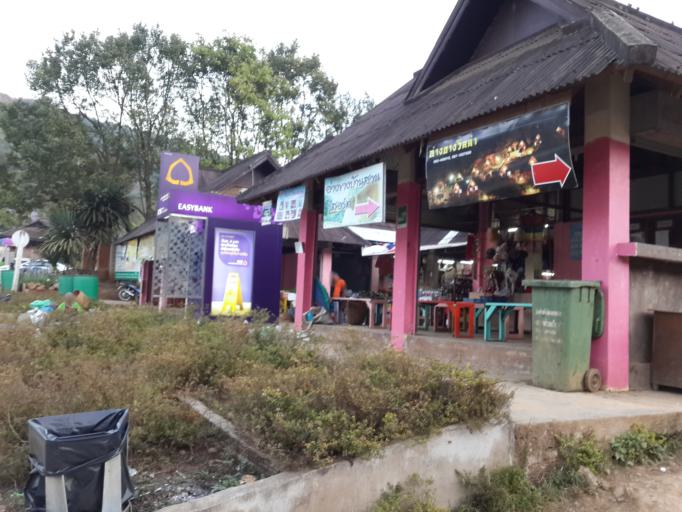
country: TH
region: Chiang Mai
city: Fang
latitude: 19.9005
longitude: 99.0398
